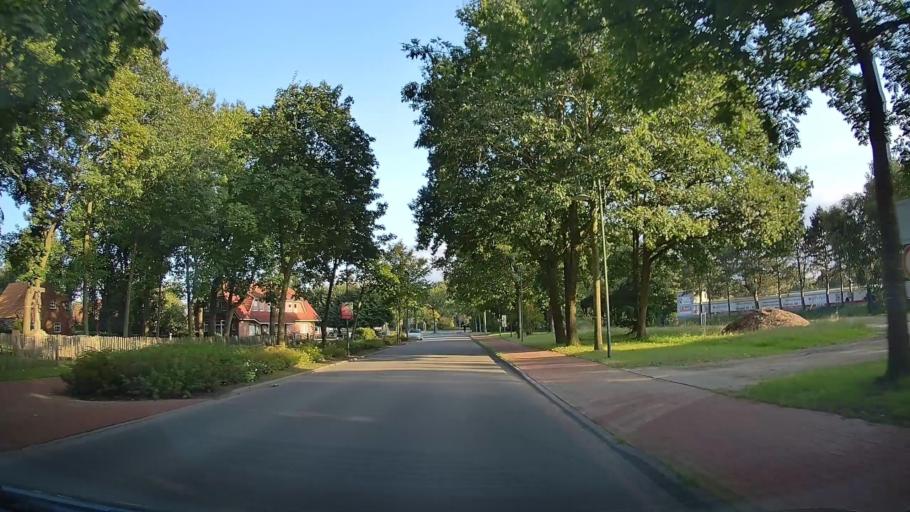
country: DE
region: Lower Saxony
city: Hilkenbrook
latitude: 53.0373
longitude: 7.7443
